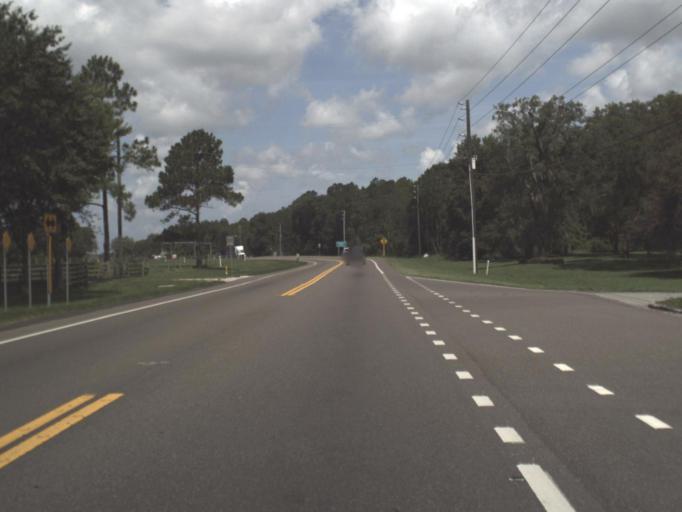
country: US
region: Florida
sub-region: Pasco County
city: Shady Hills
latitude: 28.3297
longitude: -82.5376
